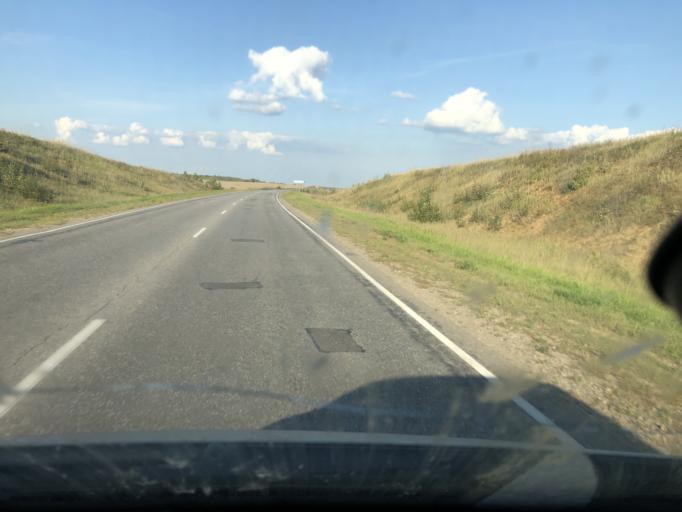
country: RU
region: Kaluga
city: Kozel'sk
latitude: 54.0815
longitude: 35.8157
